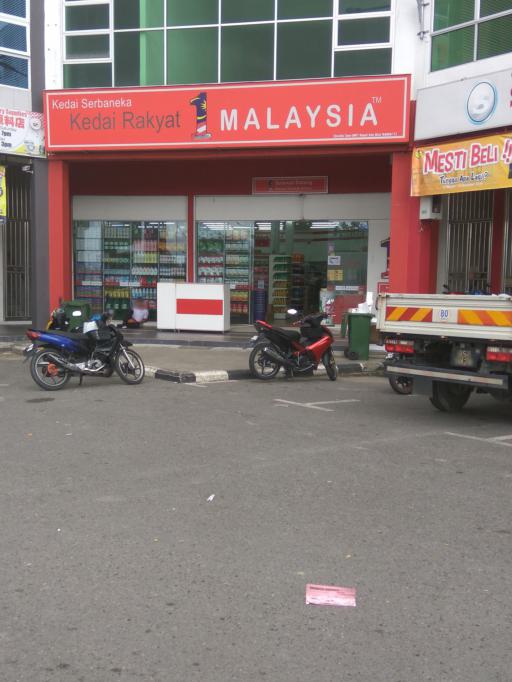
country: MY
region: Sarawak
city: Sibu
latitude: 2.2674
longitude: 111.8616
